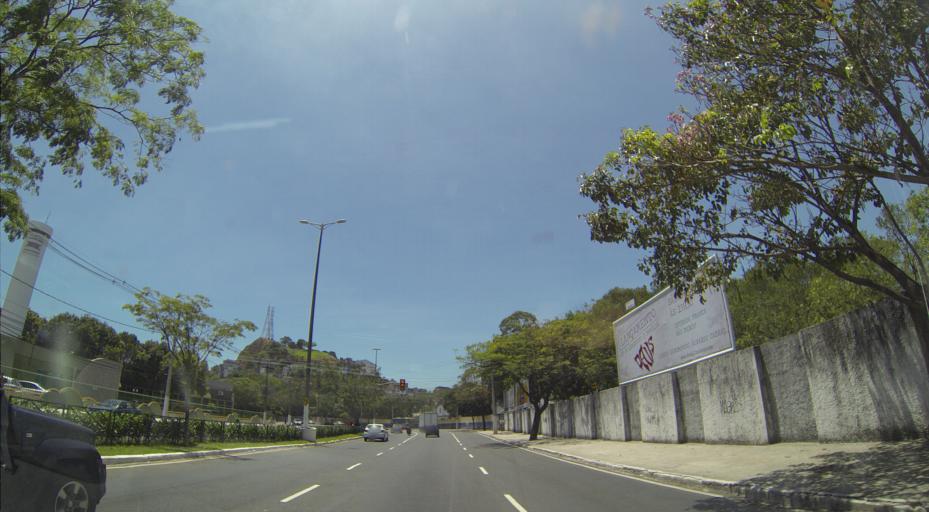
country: BR
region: Espirito Santo
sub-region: Vila Velha
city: Vila Velha
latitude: -20.3184
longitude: -40.3081
